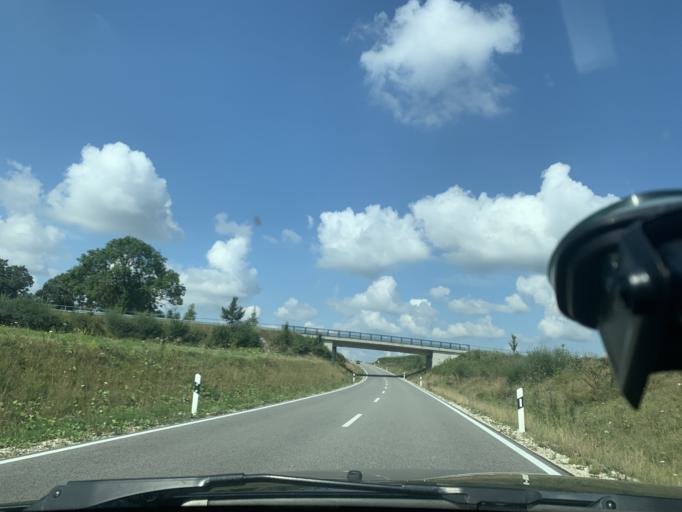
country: DE
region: Bavaria
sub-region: Upper Bavaria
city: Egenhofen
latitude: 48.3007
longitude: 11.1627
